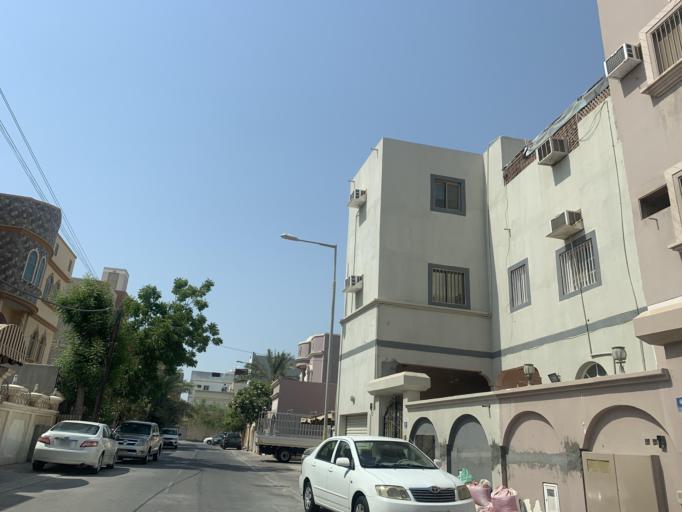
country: BH
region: Manama
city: Jidd Hafs
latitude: 26.2017
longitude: 50.5306
